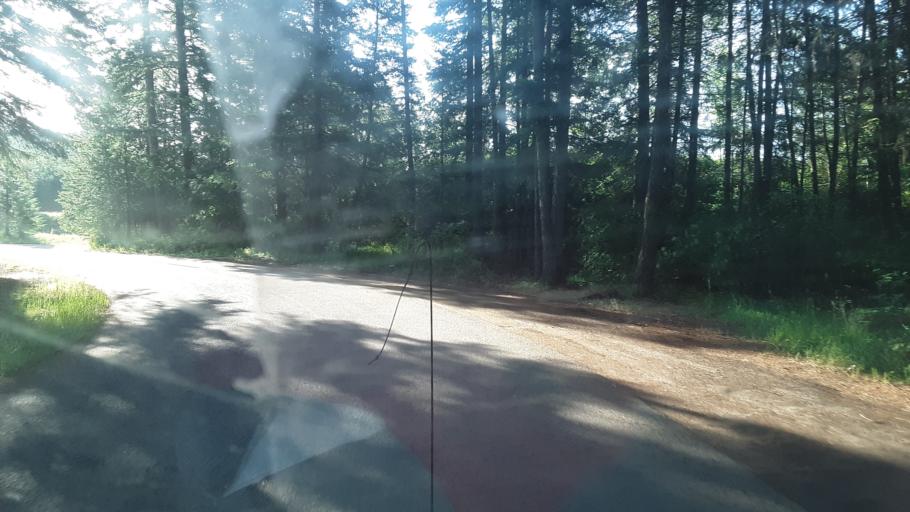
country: US
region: Idaho
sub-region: Boundary County
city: Bonners Ferry
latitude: 48.7262
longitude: -116.1764
